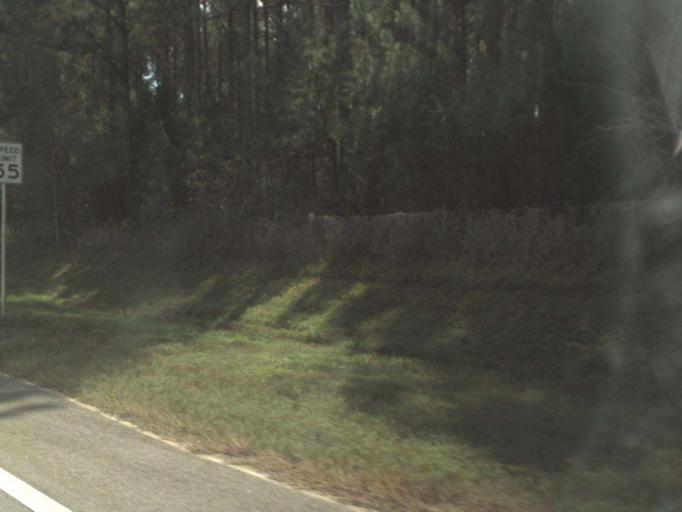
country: US
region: Florida
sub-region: Jackson County
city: Marianna
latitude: 30.8375
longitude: -85.3425
